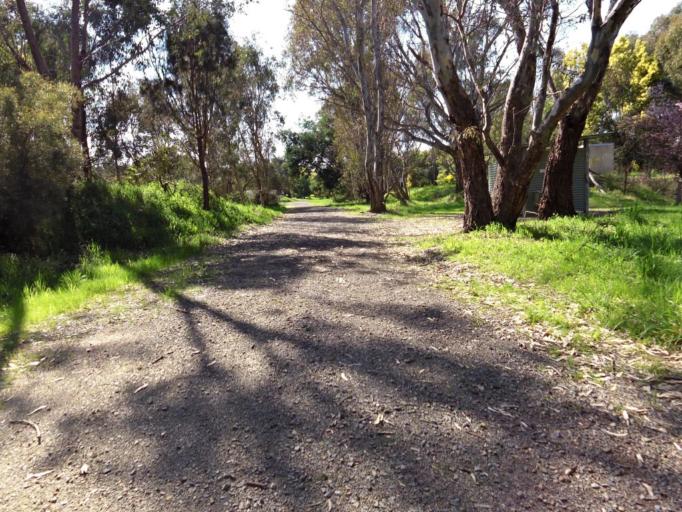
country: AU
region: Victoria
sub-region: Murrindindi
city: Alexandra
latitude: -37.1506
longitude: 145.5826
